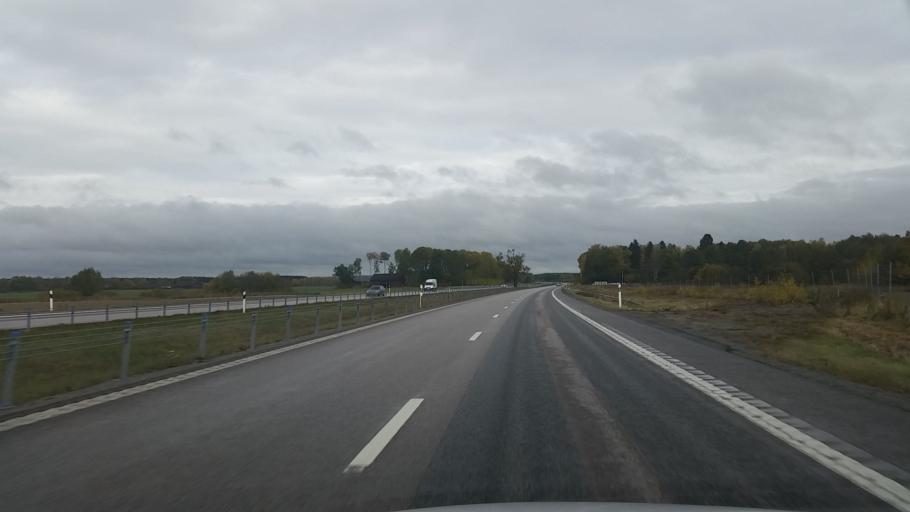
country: SE
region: Uppsala
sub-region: Osthammars Kommun
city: Bjorklinge
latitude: 60.0576
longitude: 17.6146
